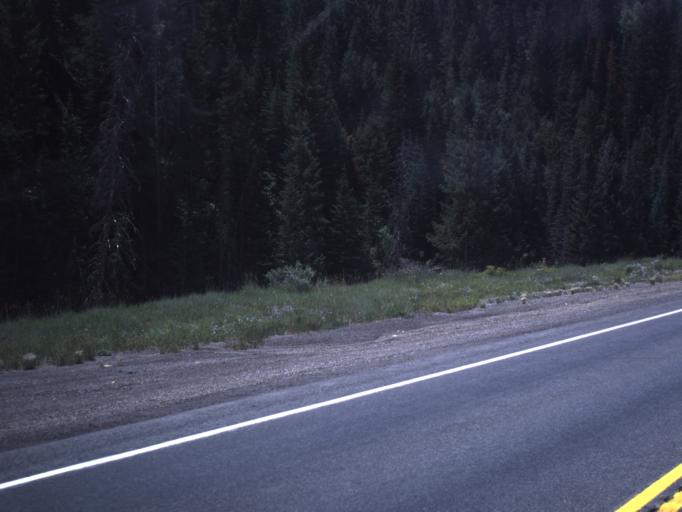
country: US
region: Utah
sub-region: Sanpete County
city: Fairview
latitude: 39.6838
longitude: -111.1664
